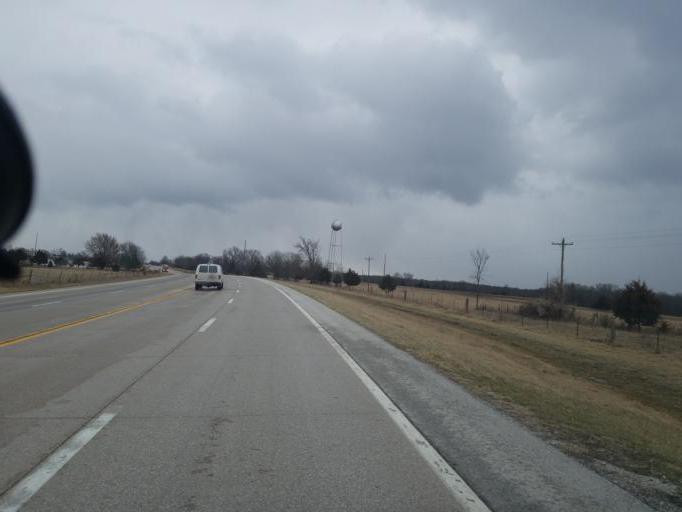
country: US
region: Missouri
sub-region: Macon County
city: Macon
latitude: 39.7838
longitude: -92.4815
